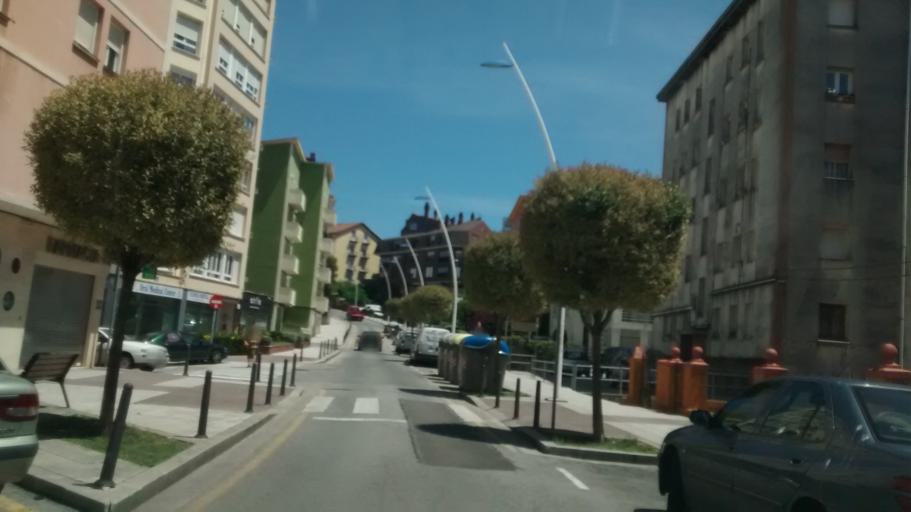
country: ES
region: Cantabria
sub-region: Provincia de Cantabria
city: Santander
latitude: 43.4653
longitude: -3.7889
